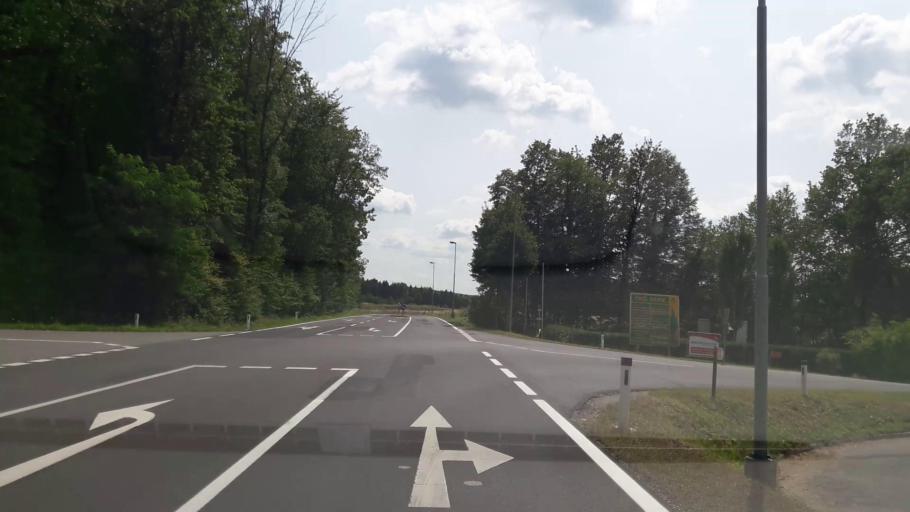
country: AT
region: Styria
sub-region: Politischer Bezirk Hartberg-Fuerstenfeld
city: Hartberg
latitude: 47.2588
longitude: 15.9730
